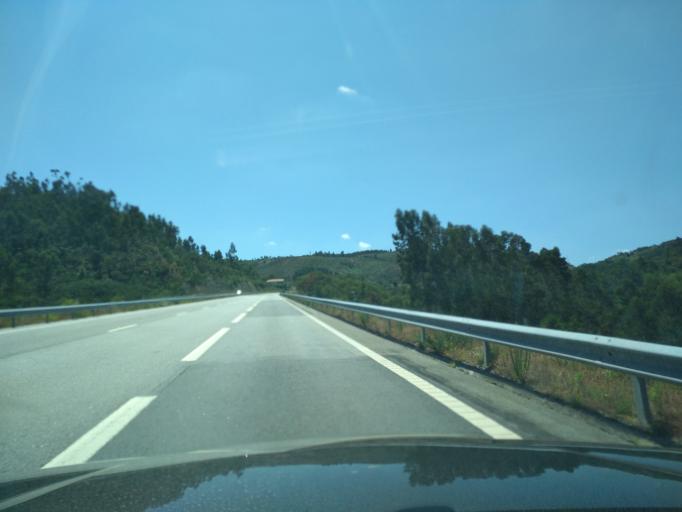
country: PT
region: Braga
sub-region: Celorico de Basto
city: Celorico de Basto
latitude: 41.4497
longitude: -8.0506
